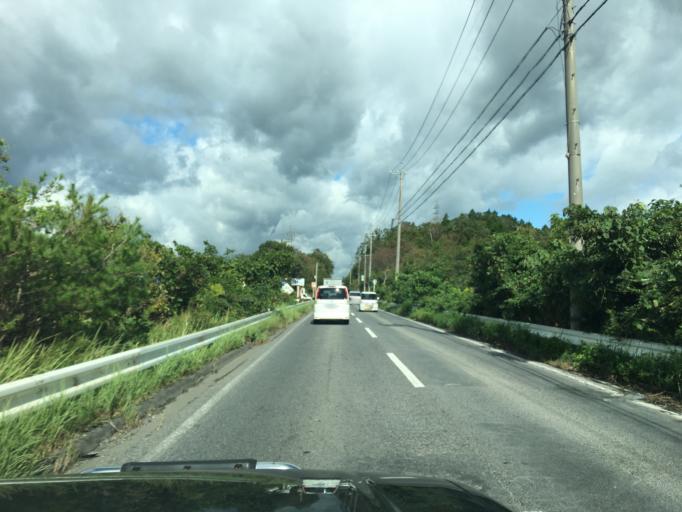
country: JP
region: Mie
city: Ueno-ebisumachi
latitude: 34.8125
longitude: 136.1840
